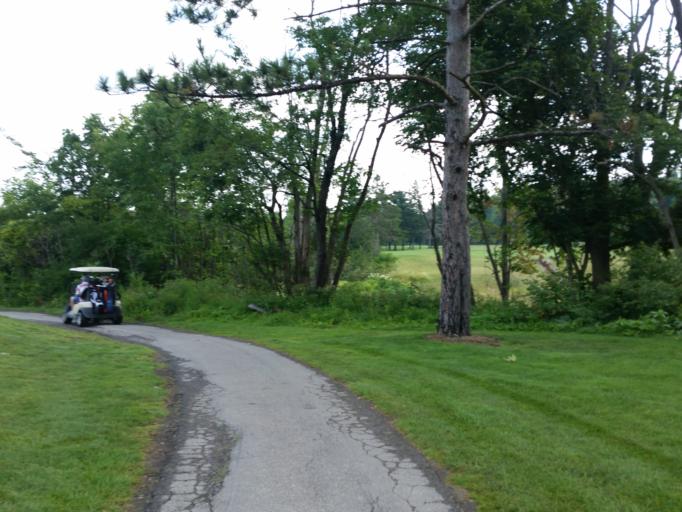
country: US
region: Ohio
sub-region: Cuyahoga County
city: North Olmsted
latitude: 41.4027
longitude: -81.9100
